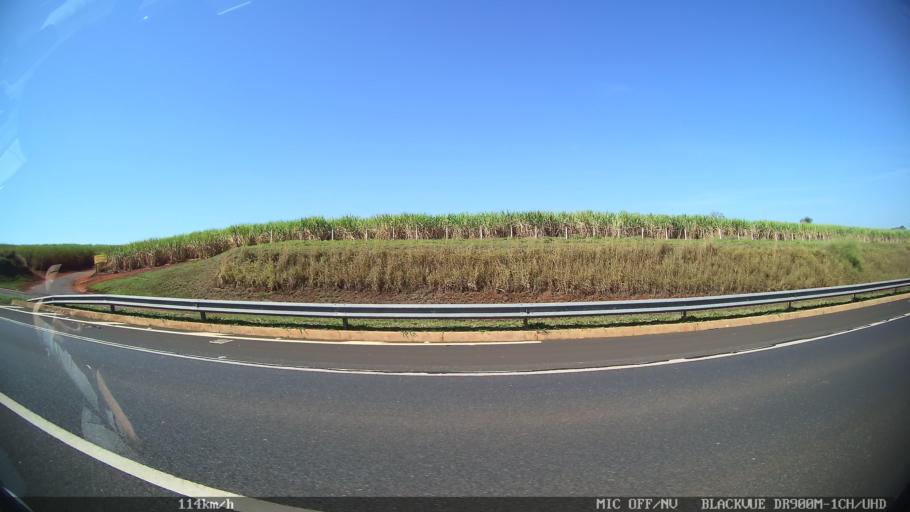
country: BR
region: Sao Paulo
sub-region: Batatais
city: Batatais
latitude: -20.7856
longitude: -47.5550
